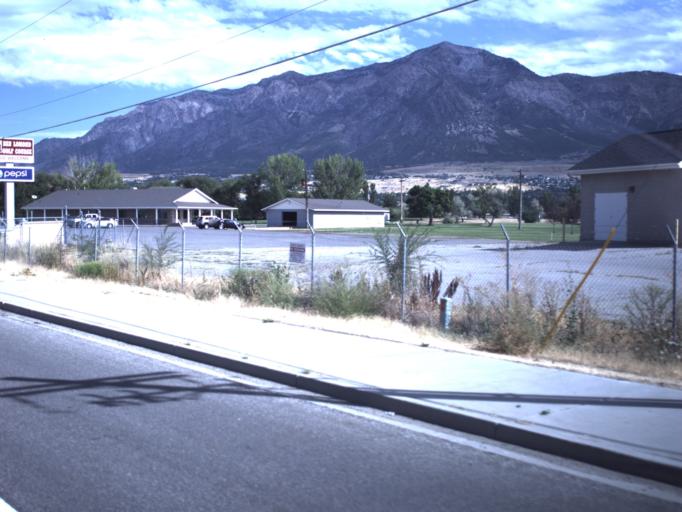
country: US
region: Utah
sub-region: Weber County
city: Harrisville
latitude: 41.2902
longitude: -111.9915
